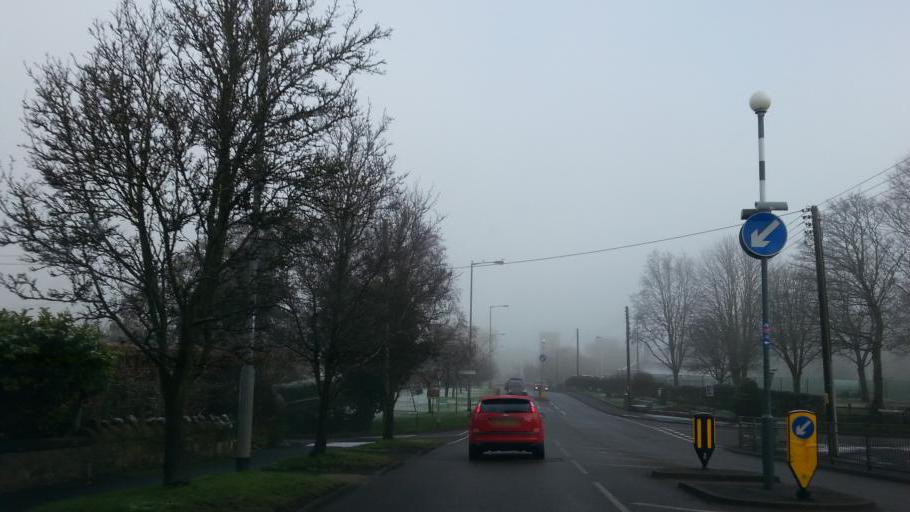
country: GB
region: England
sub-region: Staffordshire
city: Biddulph
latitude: 53.1261
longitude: -2.1676
